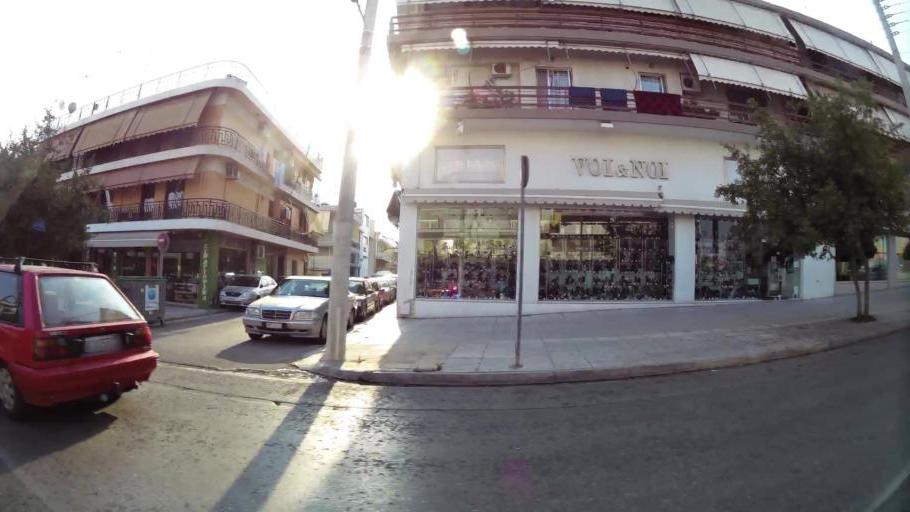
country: GR
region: Attica
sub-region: Nomarchia Athinas
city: Ilion
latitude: 38.0344
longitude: 23.6956
